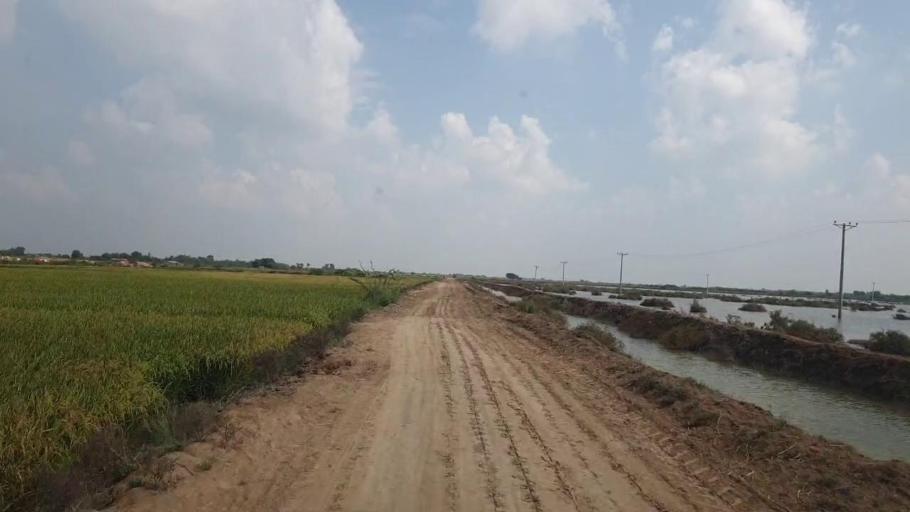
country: PK
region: Sindh
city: Badin
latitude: 24.5328
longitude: 68.6280
